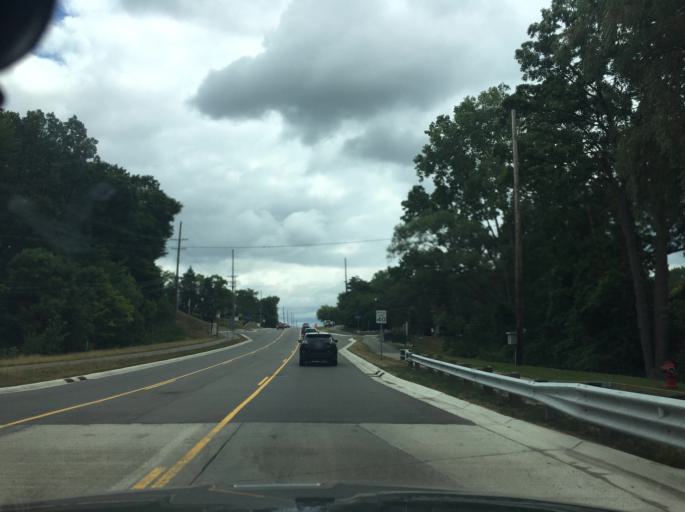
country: US
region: Michigan
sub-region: Oakland County
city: Rochester
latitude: 42.6954
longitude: -83.1461
